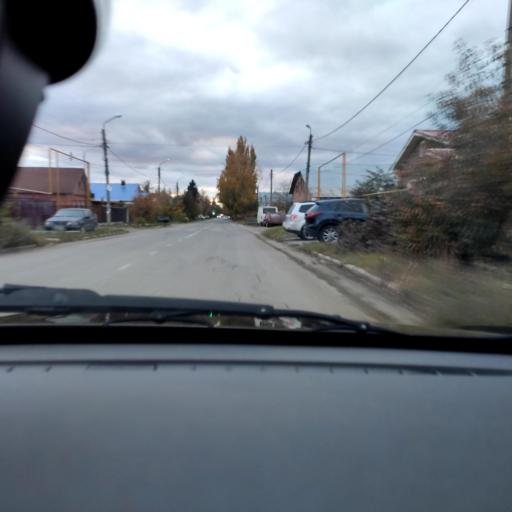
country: RU
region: Samara
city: Tol'yatti
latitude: 53.5367
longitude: 49.4224
